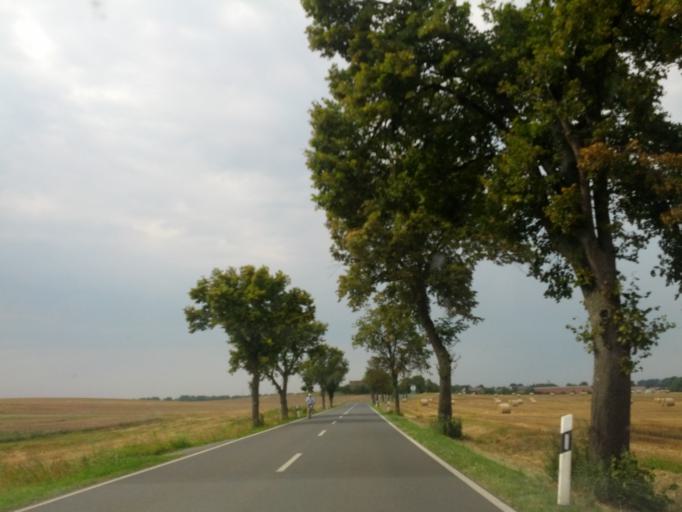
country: DE
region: Brandenburg
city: Fehrbellin
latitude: 52.7865
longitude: 12.8190
